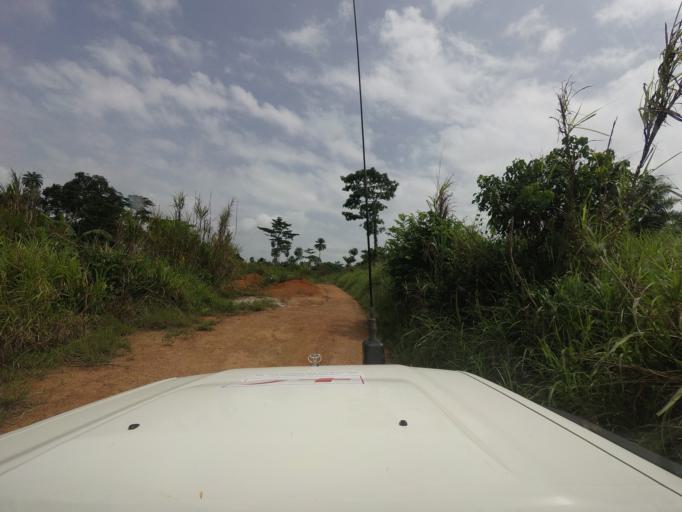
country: GN
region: Nzerekore
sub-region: Nzerekore Prefecture
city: Nzerekore
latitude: 7.7404
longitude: -8.7542
